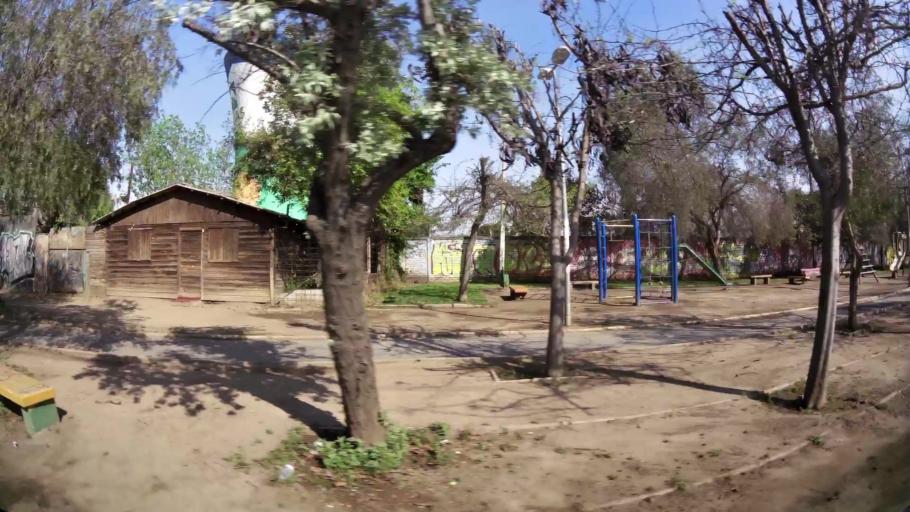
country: CL
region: Santiago Metropolitan
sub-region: Provincia de Santiago
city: Lo Prado
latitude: -33.4257
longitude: -70.7305
